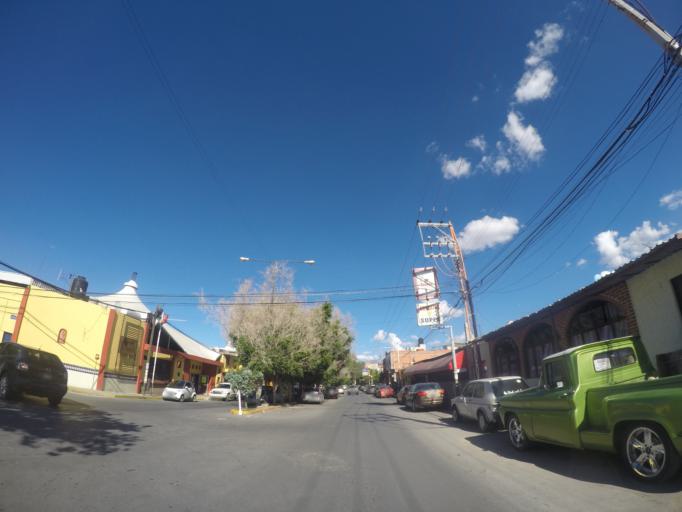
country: MX
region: San Luis Potosi
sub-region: San Luis Potosi
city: San Luis Potosi
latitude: 22.1512
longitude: -101.0212
